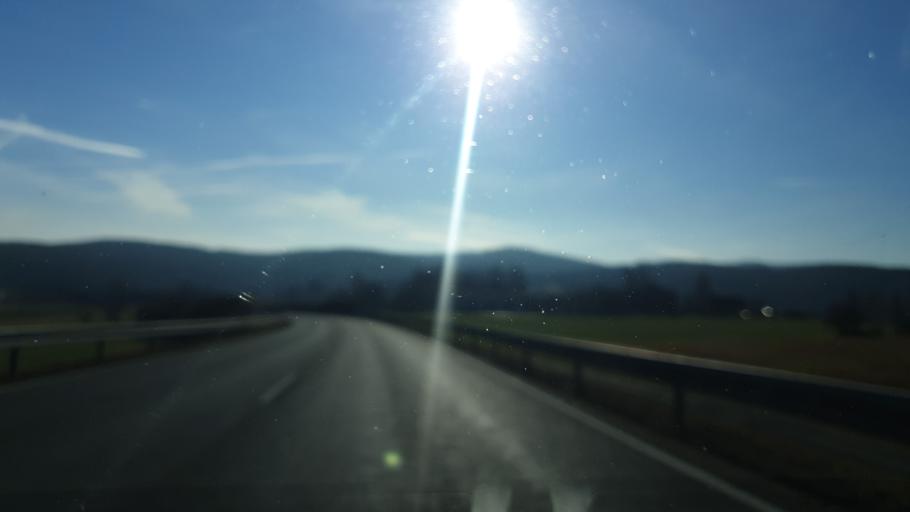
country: DE
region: Saxony
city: Bad Brambach
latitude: 50.2271
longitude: 12.3199
